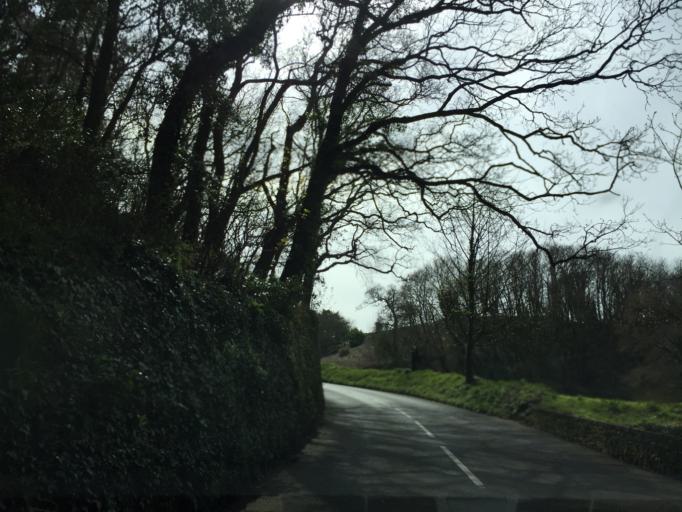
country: JE
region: St Helier
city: Saint Helier
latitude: 49.2439
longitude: -2.2030
